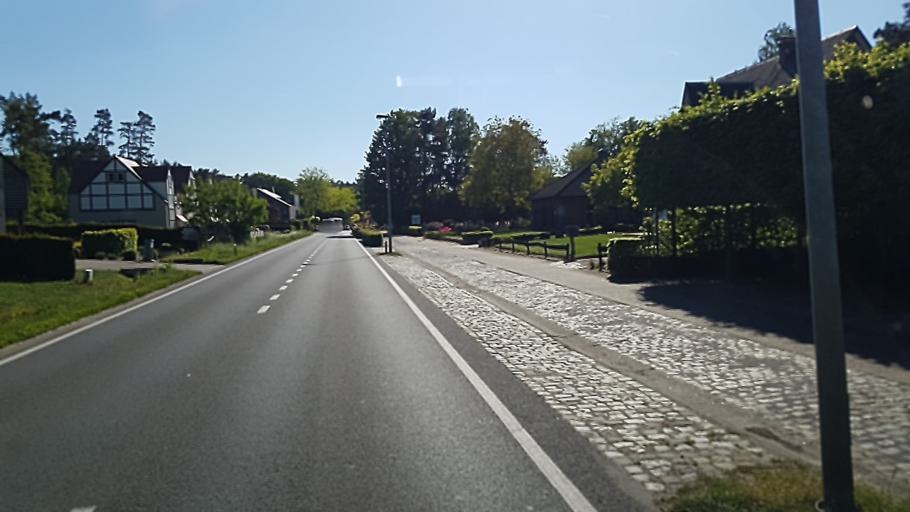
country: BE
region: Flanders
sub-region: Provincie Antwerpen
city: Kasterlee
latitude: 51.2279
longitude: 4.9310
